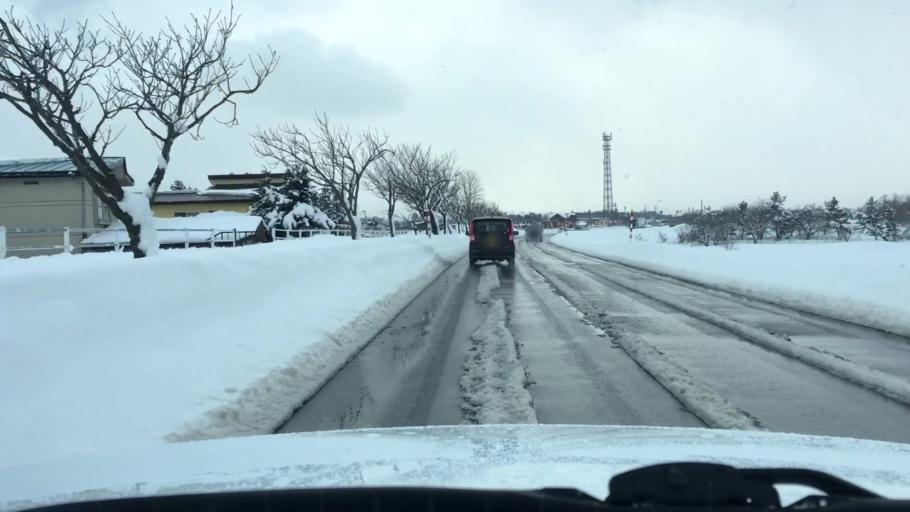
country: JP
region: Aomori
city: Hirosaki
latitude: 40.6243
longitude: 140.4734
